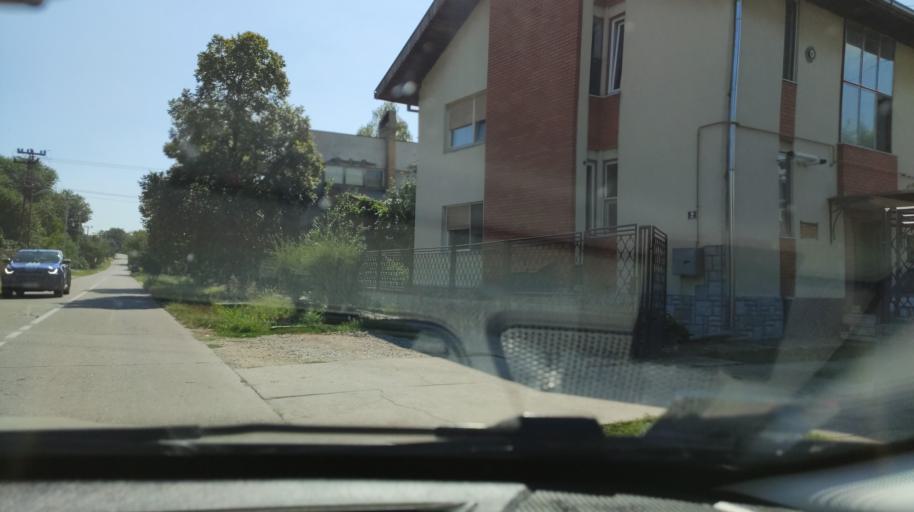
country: RS
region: Autonomna Pokrajina Vojvodina
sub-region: Severnobacki Okrug
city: Backa Topola
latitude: 45.8217
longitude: 19.6329
